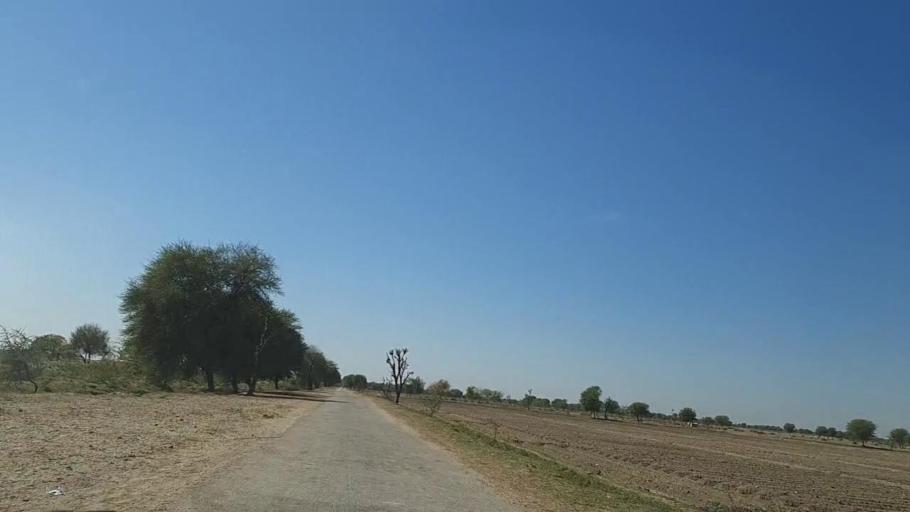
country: PK
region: Sindh
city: Dhoro Naro
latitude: 25.5227
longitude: 69.5213
